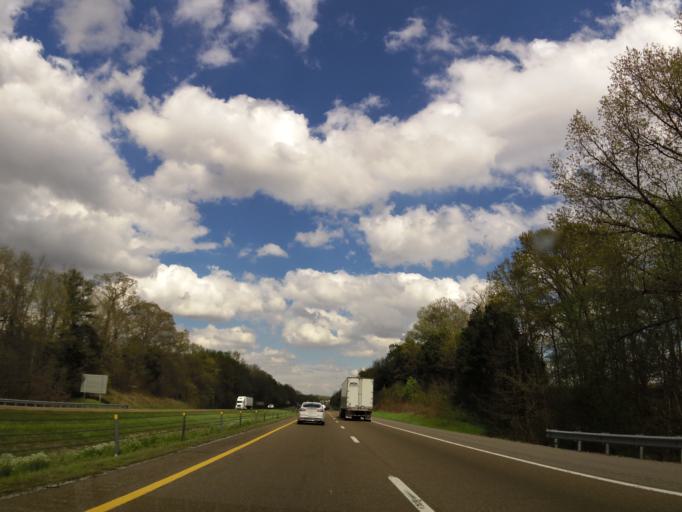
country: US
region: Tennessee
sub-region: Crockett County
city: Bells
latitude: 35.6046
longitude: -89.0353
